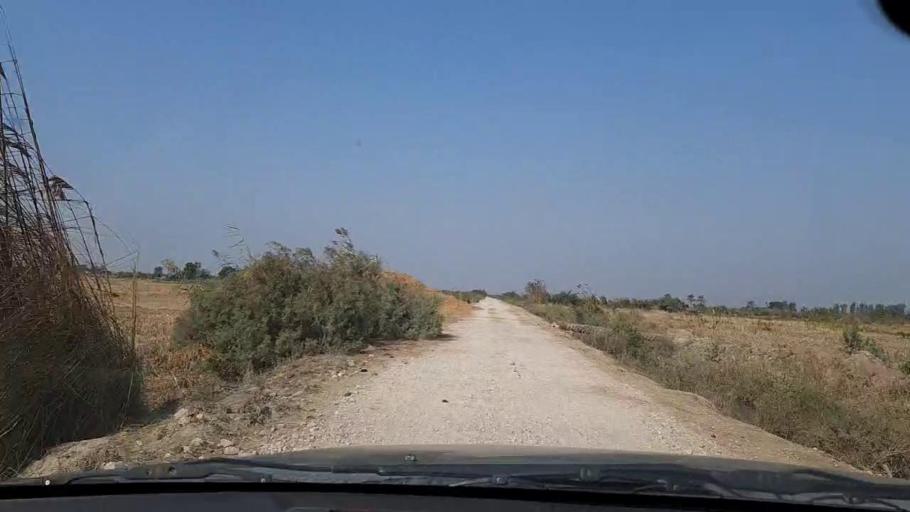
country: PK
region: Sindh
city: Mirpur Sakro
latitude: 24.3722
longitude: 67.6830
